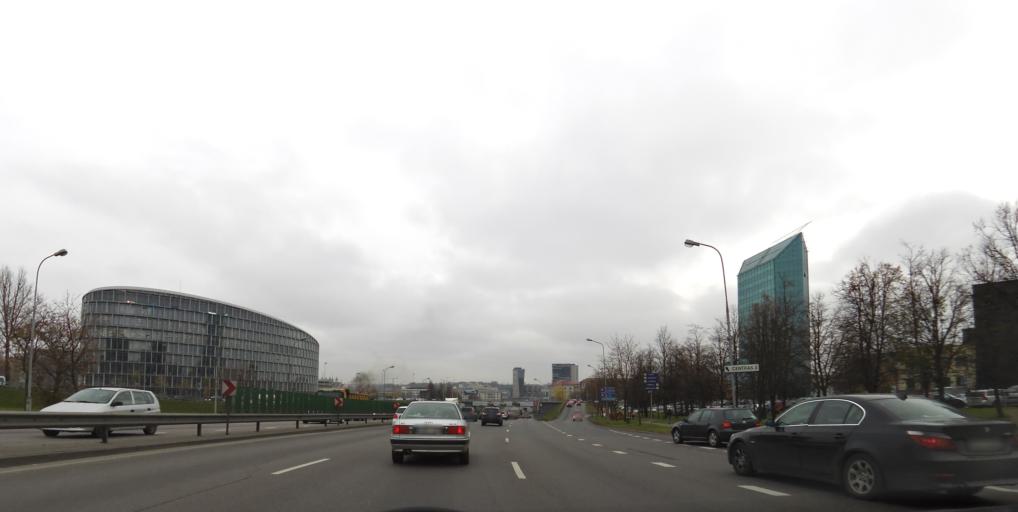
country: LT
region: Vilnius County
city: Seskine
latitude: 54.7013
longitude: 25.2631
